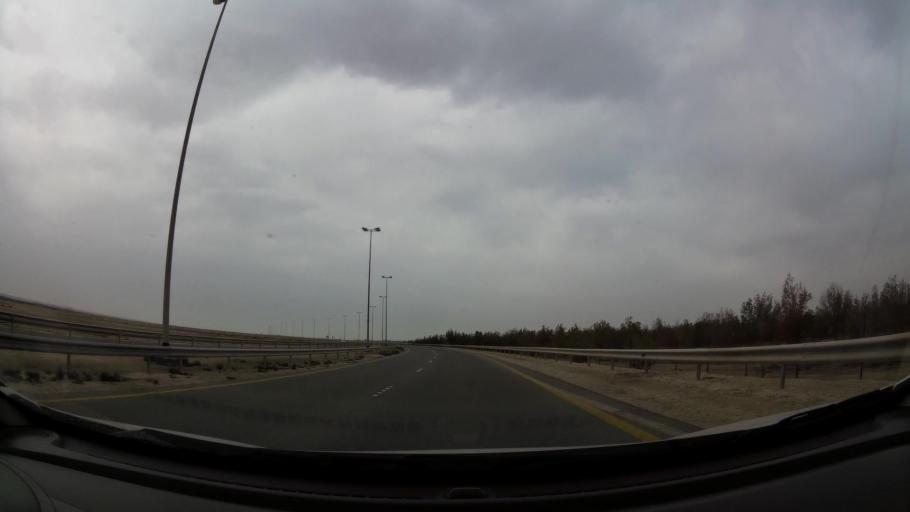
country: BH
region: Central Governorate
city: Dar Kulayb
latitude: 26.0134
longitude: 50.4837
